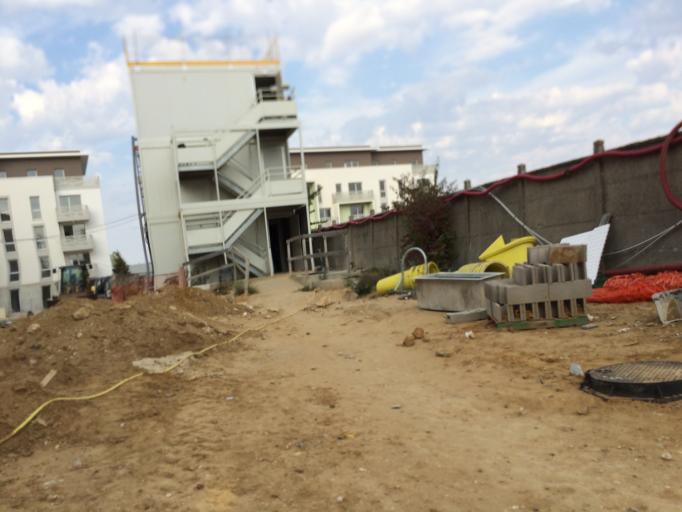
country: FR
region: Ile-de-France
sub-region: Departement de l'Essonne
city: Montlhery
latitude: 48.6443
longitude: 2.2718
